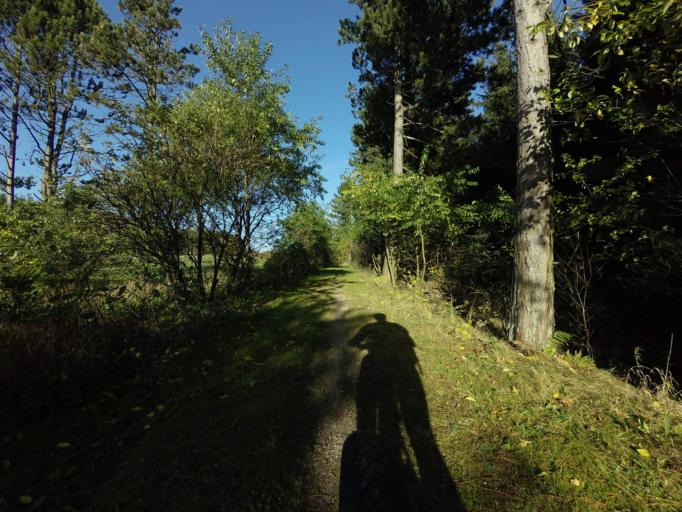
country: DK
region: Central Jutland
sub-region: Syddjurs Kommune
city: Ryomgard
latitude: 56.4741
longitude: 10.6406
